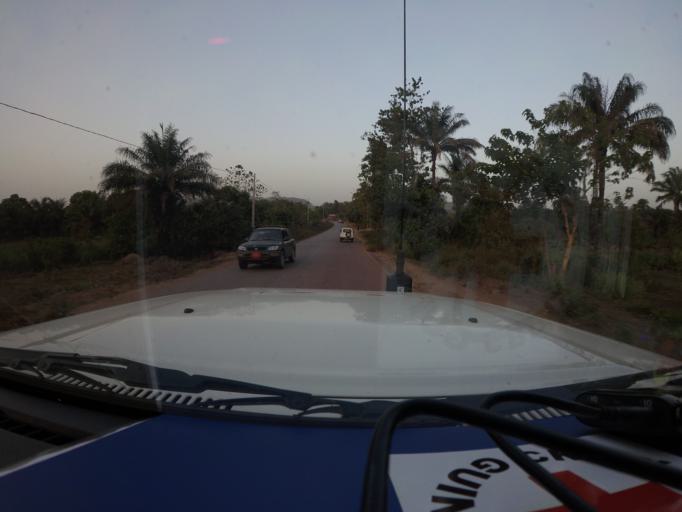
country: GN
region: Kindia
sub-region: Kindia
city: Kindia
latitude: 9.8546
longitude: -13.0854
